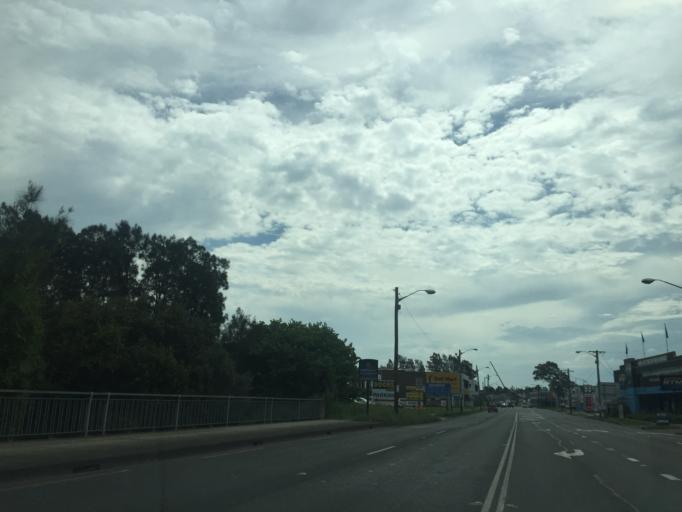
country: AU
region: New South Wales
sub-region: Parramatta
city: Granville
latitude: -33.8359
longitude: 151.0233
